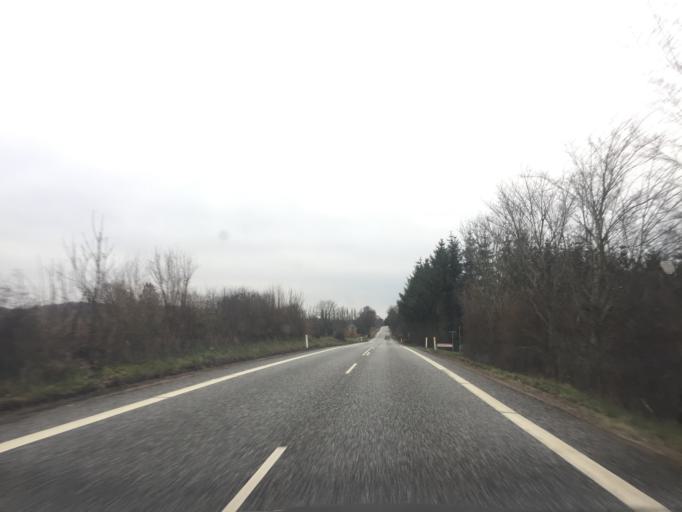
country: DK
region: South Denmark
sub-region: Svendborg Kommune
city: Thuro By
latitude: 55.1158
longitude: 10.6541
